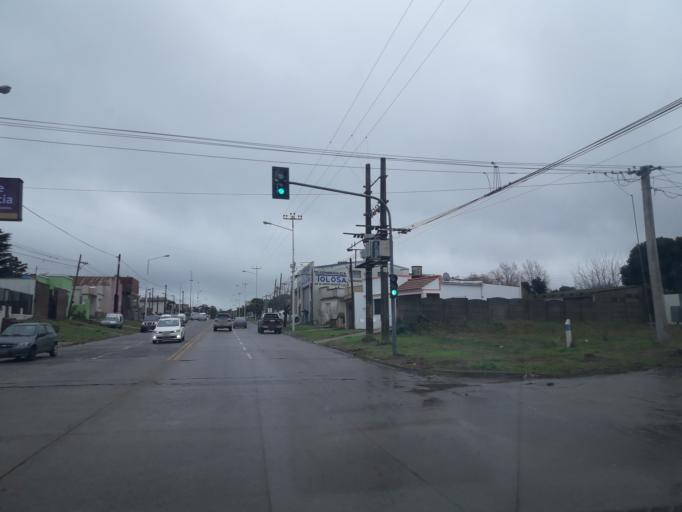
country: AR
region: Buenos Aires
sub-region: Partido de Tandil
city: Tandil
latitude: -37.3192
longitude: -59.1601
